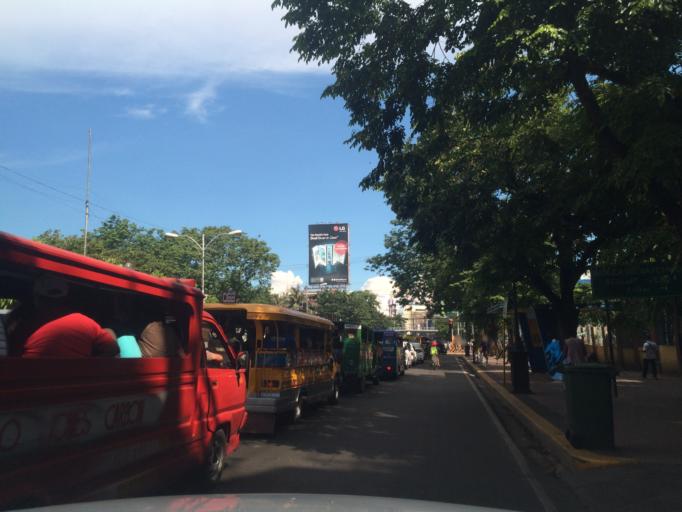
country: PH
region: Central Visayas
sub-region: Cebu City
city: Calero
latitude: 10.3004
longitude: 123.8964
